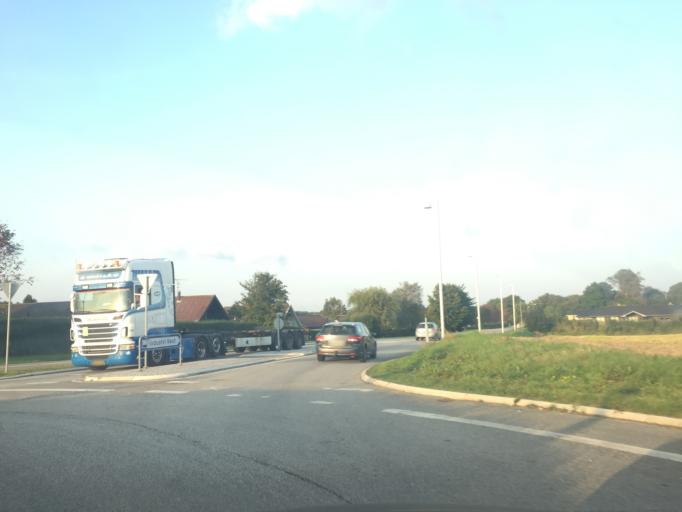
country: DK
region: Zealand
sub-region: Lejre Kommune
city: Kirke Hvalso
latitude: 55.5860
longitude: 11.8571
